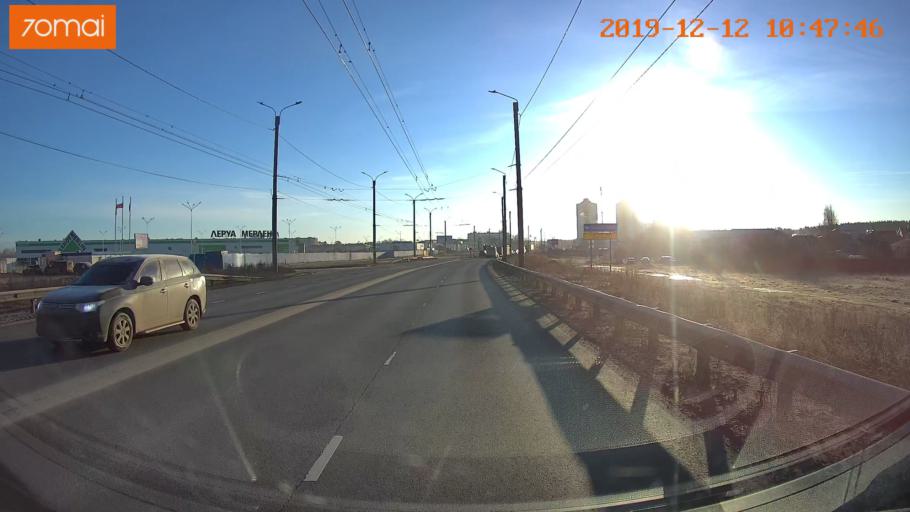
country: RU
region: Ivanovo
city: Kokhma
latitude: 56.9472
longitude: 41.0540
